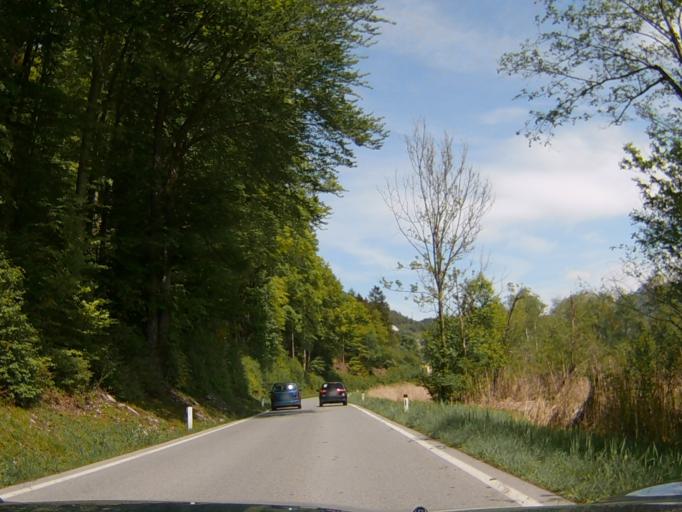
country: AT
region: Tyrol
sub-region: Politischer Bezirk Schwaz
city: Buch bei Jenbach
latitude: 47.3879
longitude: 11.7510
